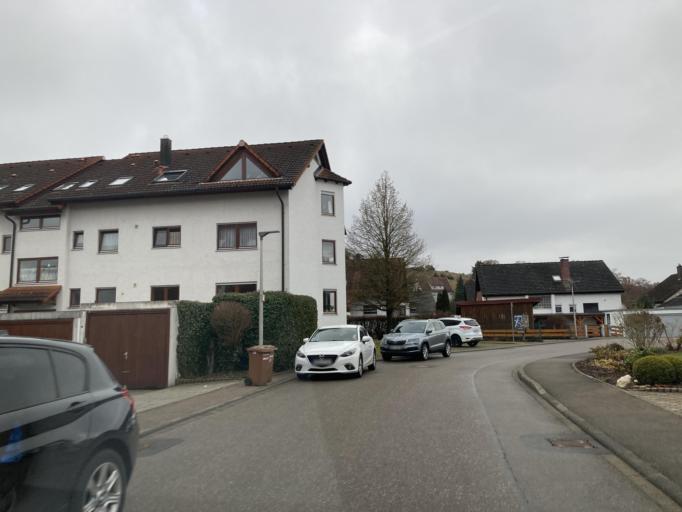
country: DE
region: Baden-Wuerttemberg
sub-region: Regierungsbezirk Stuttgart
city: Bolheim
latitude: 48.6235
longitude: 10.1615
